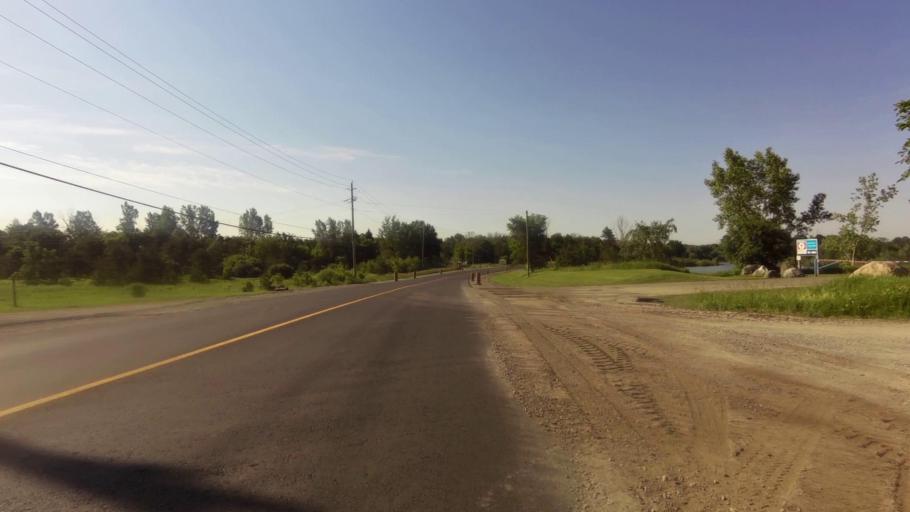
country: CA
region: Ontario
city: Ottawa
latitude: 45.2141
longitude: -75.5688
